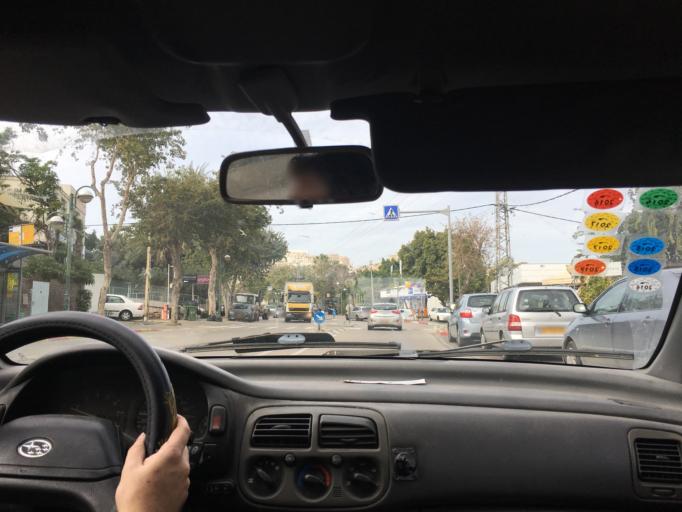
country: IL
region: Tel Aviv
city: Ramat HaSharon
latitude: 32.1364
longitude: 34.8443
